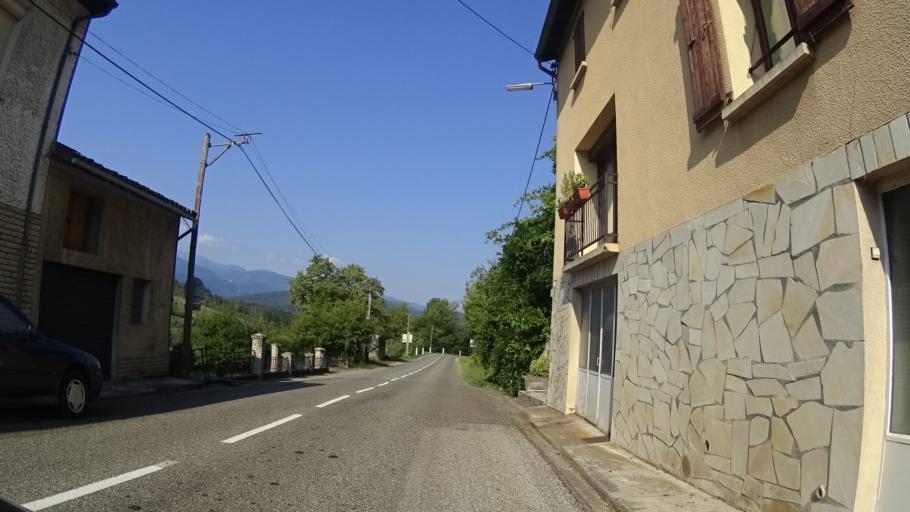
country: FR
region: Midi-Pyrenees
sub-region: Departement de l'Ariege
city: Belesta
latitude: 42.9111
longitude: 1.9634
